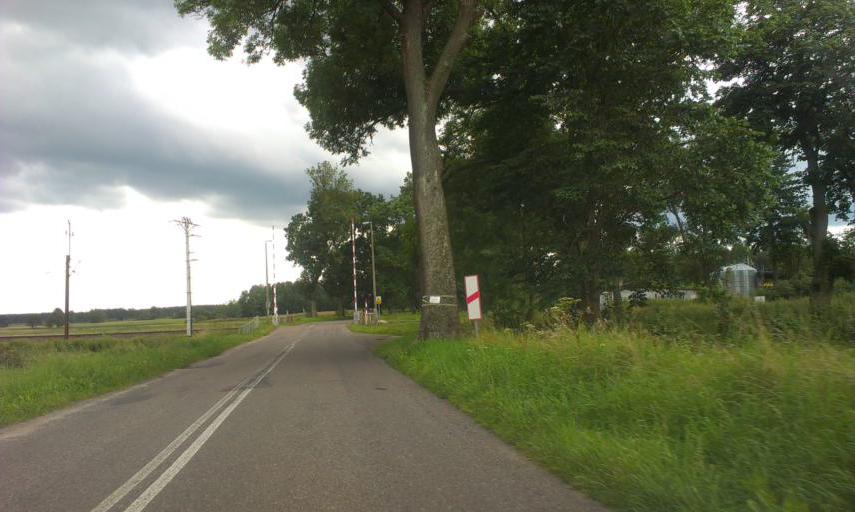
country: PL
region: West Pomeranian Voivodeship
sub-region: Powiat bialogardzki
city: Tychowo
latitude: 53.9218
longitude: 16.2425
